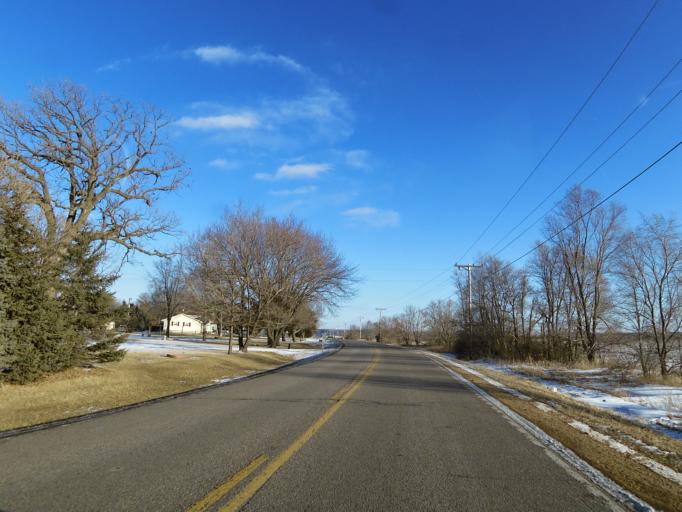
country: US
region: Minnesota
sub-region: Scott County
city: Prior Lake
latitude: 44.7729
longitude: -93.4559
